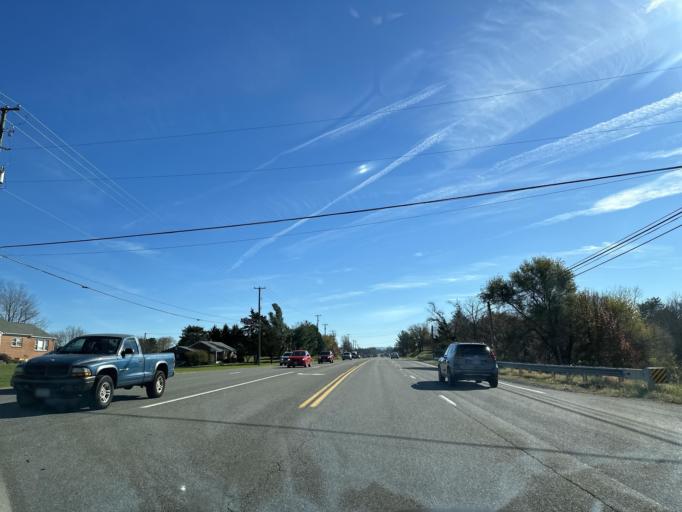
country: US
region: Virginia
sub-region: Augusta County
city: Fishersville
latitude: 38.1116
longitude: -79.0034
